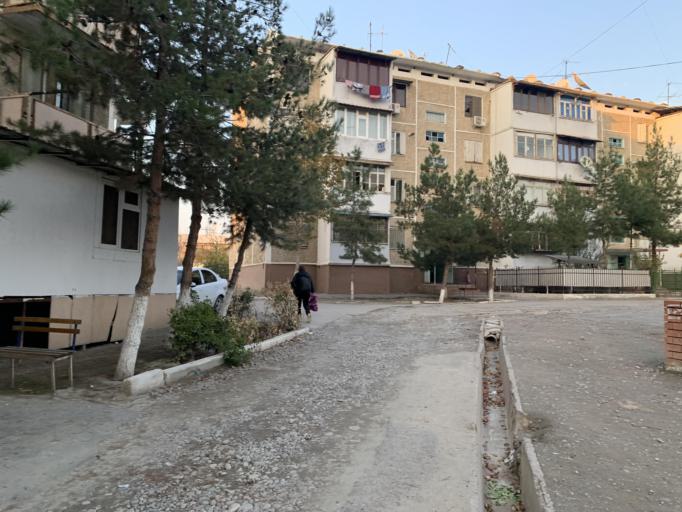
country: UZ
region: Namangan
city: Namangan Shahri
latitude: 41.0057
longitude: 71.5984
